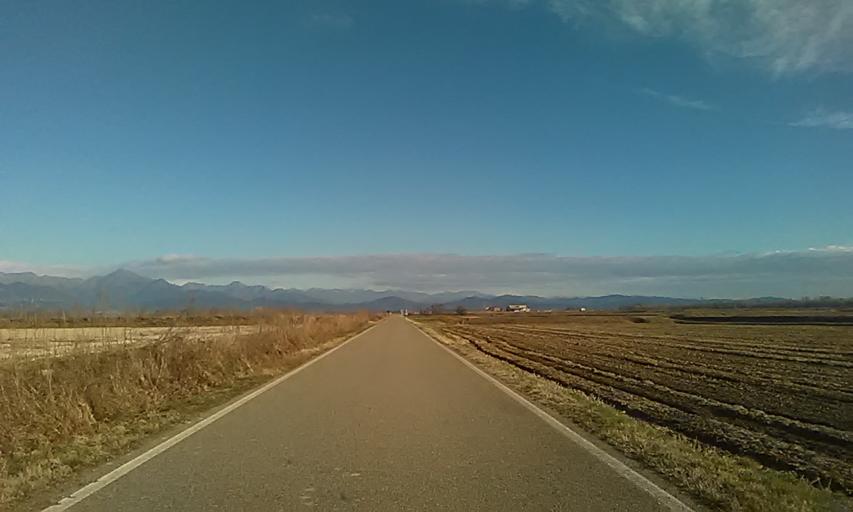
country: IT
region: Piedmont
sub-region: Provincia di Vercelli
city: Buronzo
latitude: 45.5137
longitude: 8.2702
